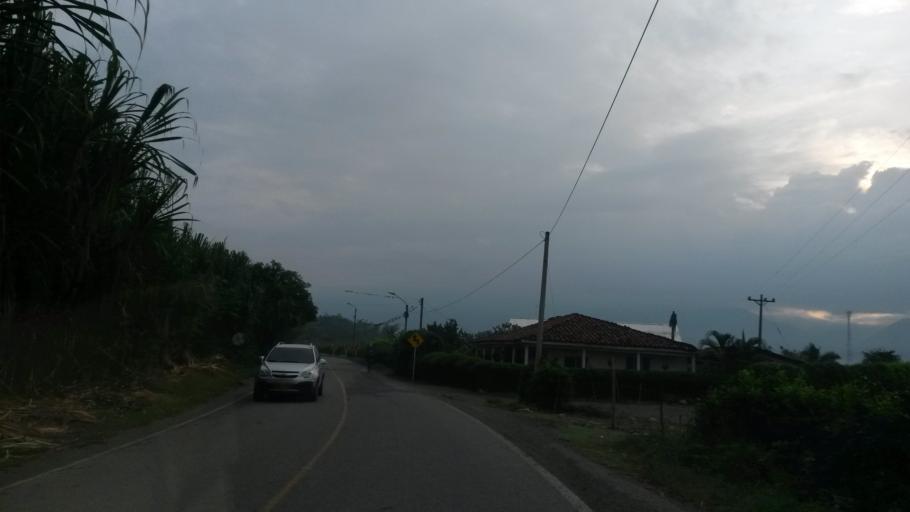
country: CO
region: Cauca
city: Padilla
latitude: 3.2275
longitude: -76.3179
